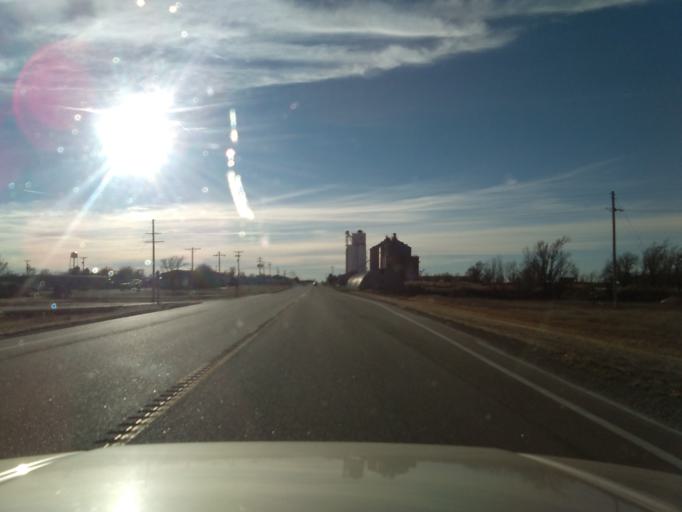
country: US
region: Kansas
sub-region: Sheridan County
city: Hoxie
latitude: 39.5463
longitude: -100.5625
